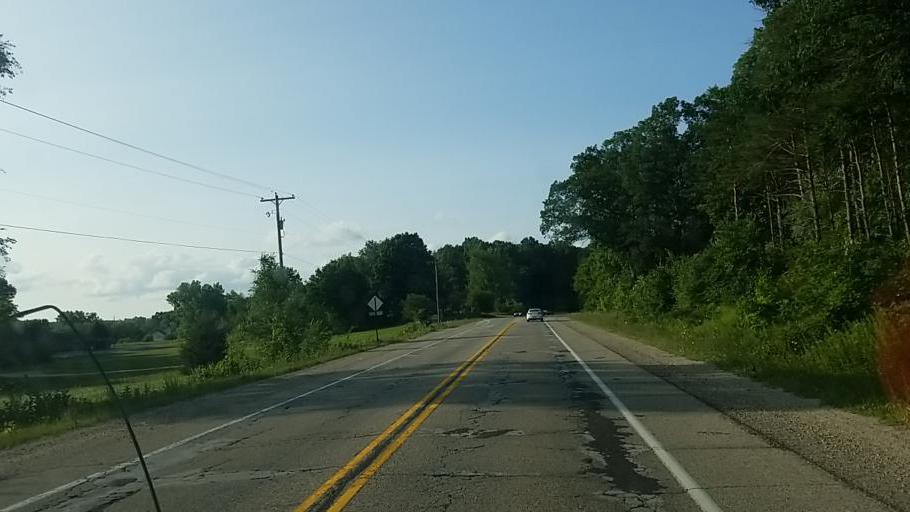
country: US
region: Michigan
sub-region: Kent County
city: Lowell
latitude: 42.9656
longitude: -85.3558
